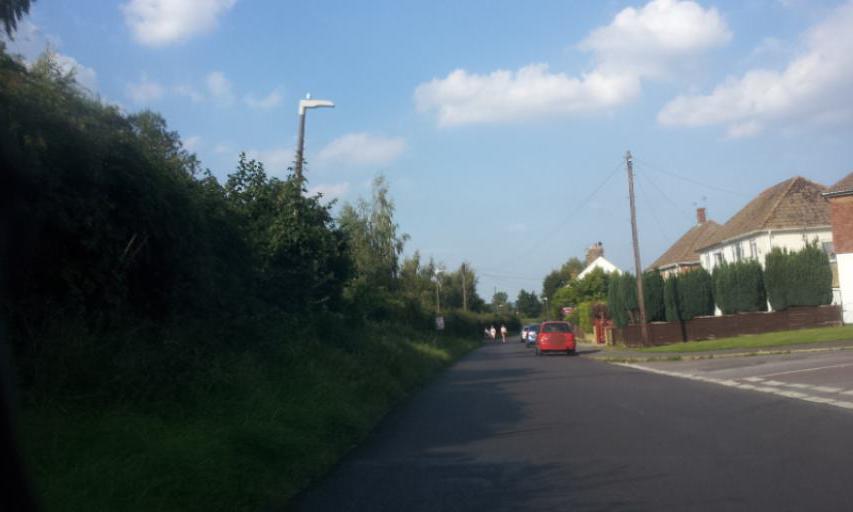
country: GB
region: England
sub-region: Kent
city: Maidstone
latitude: 51.2364
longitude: 0.4965
